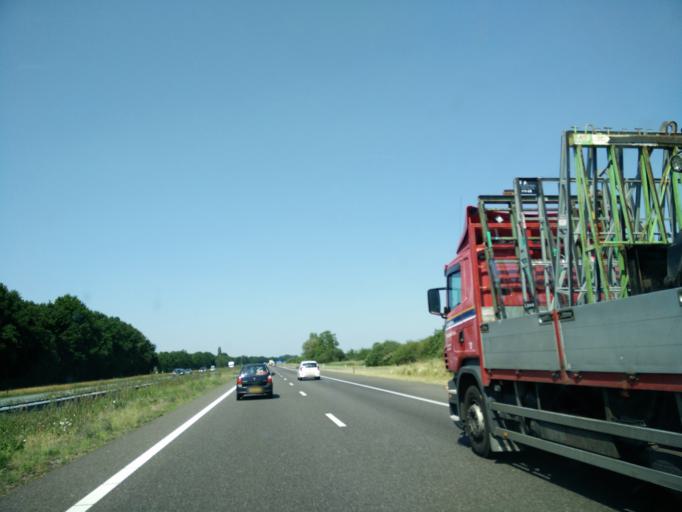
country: NL
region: Gelderland
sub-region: Gemeente Ermelo
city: Horst
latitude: 52.2949
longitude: 5.5520
